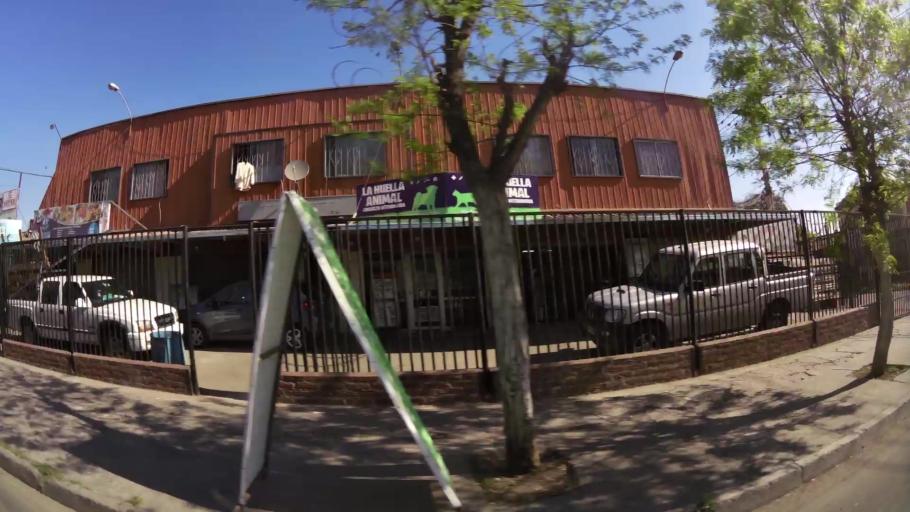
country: CL
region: Santiago Metropolitan
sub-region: Provincia de Santiago
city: Santiago
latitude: -33.5044
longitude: -70.6886
